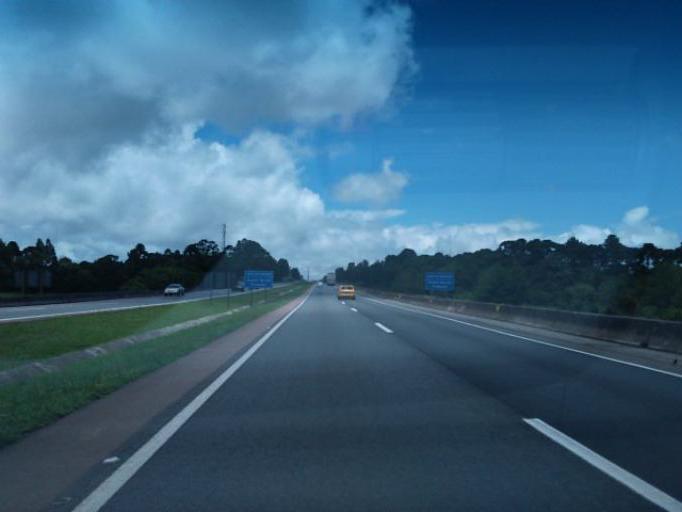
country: BR
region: Parana
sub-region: Quatro Barras
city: Quatro Barras
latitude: -25.3959
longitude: -49.0567
